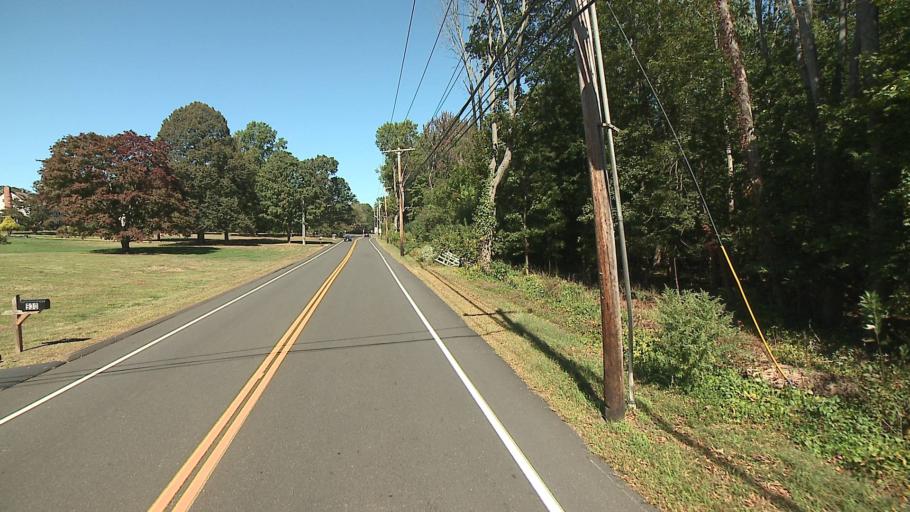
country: US
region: Connecticut
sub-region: New Haven County
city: Orange
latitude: 41.2998
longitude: -73.0258
